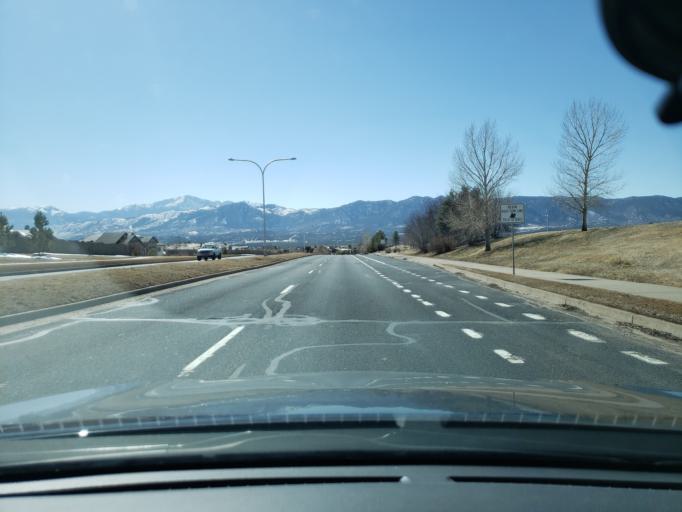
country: US
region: Colorado
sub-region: El Paso County
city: Gleneagle
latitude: 39.0289
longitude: -104.7943
